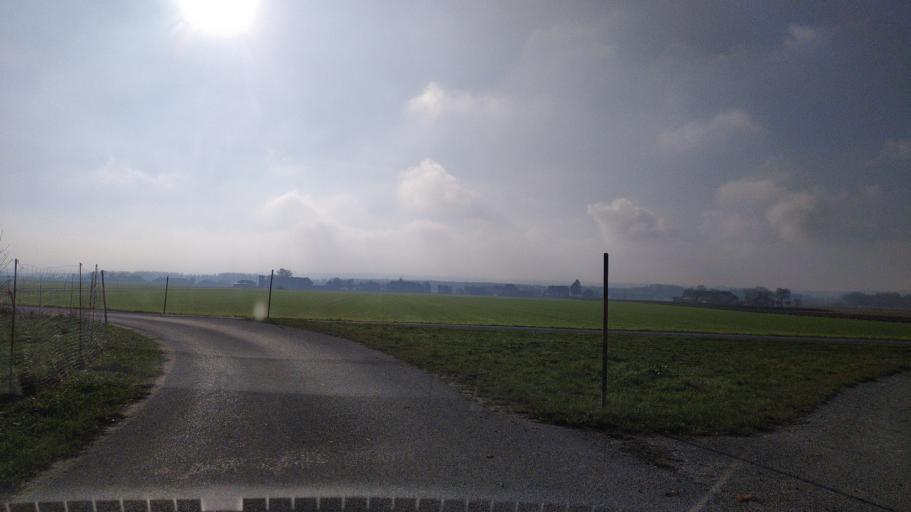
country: AT
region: Upper Austria
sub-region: Politischer Bezirk Perg
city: Perg
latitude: 48.1943
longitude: 14.6536
